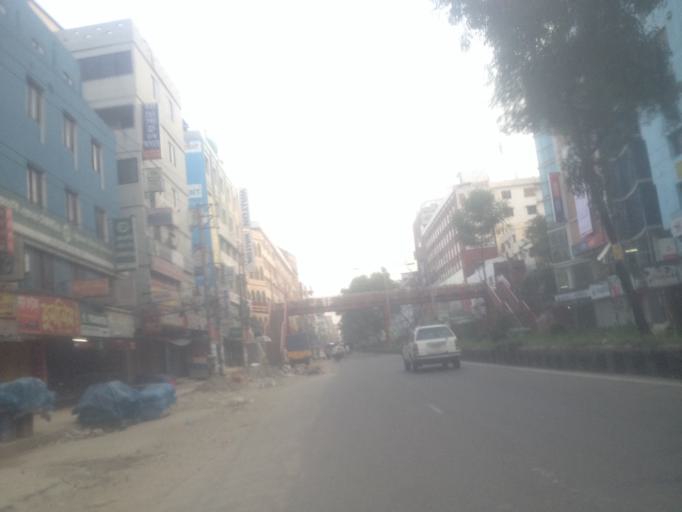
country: BD
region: Dhaka
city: Azimpur
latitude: 23.7908
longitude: 90.3755
